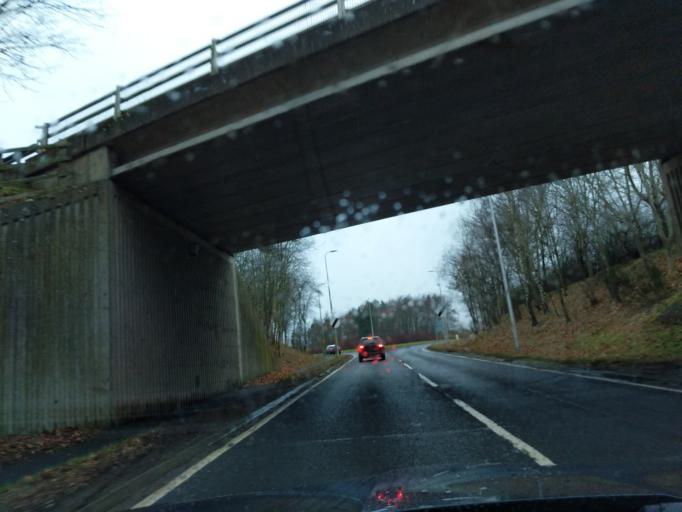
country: GB
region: Scotland
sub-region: The Scottish Borders
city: Melrose
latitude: 55.6006
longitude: -2.7492
